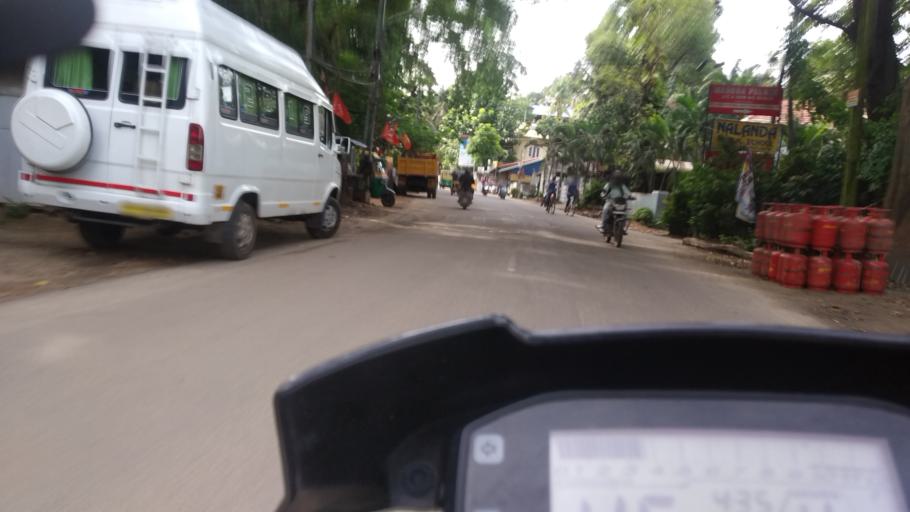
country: IN
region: Kerala
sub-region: Ernakulam
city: Cochin
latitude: 9.9834
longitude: 76.3127
